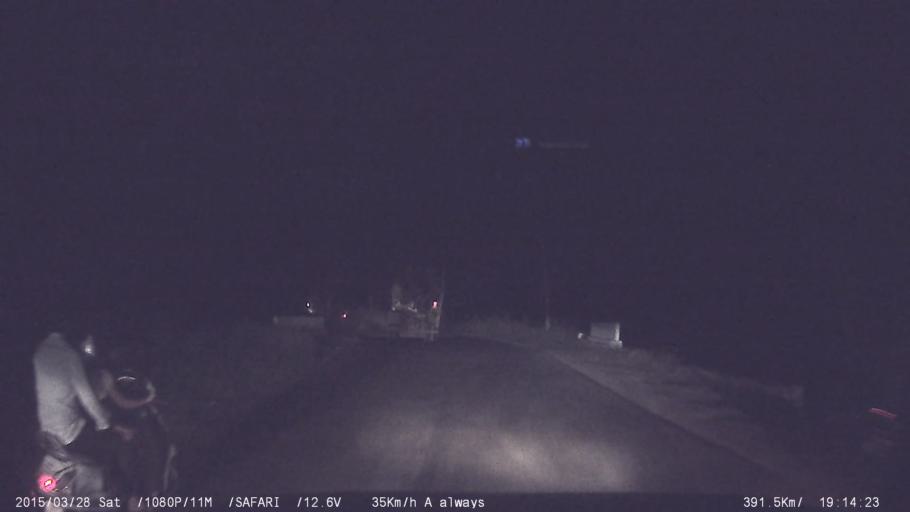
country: IN
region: Karnataka
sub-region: Mandya
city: Shrirangapattana
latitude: 12.4000
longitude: 76.6426
